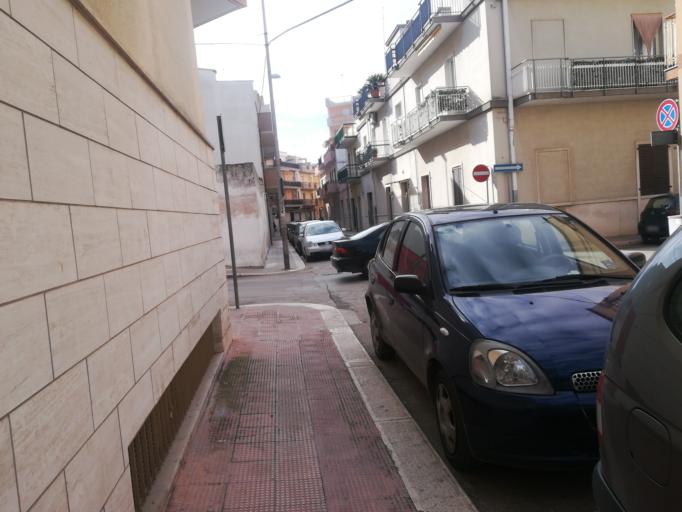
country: IT
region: Apulia
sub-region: Provincia di Barletta - Andria - Trani
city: Andria
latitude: 41.2243
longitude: 16.3043
